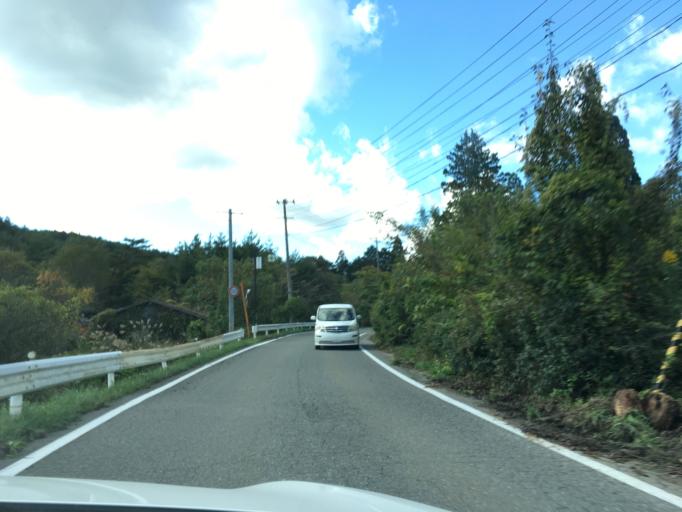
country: JP
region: Fukushima
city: Namie
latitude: 37.5630
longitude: 140.8058
